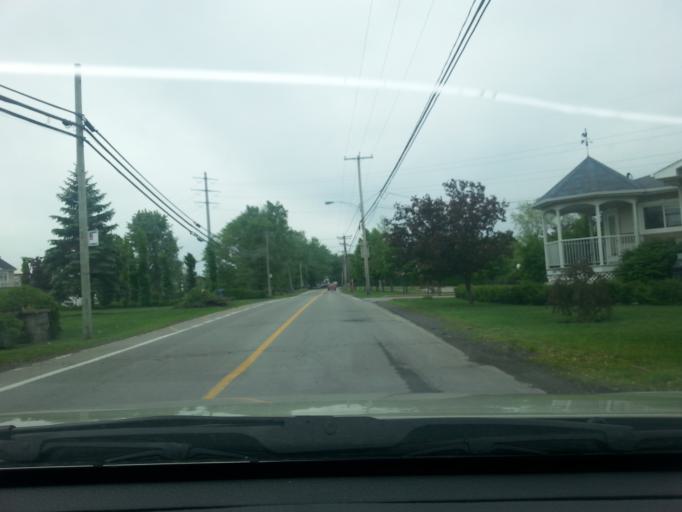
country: CA
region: Quebec
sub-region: Lanaudiere
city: Mascouche
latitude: 45.6970
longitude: -73.5821
